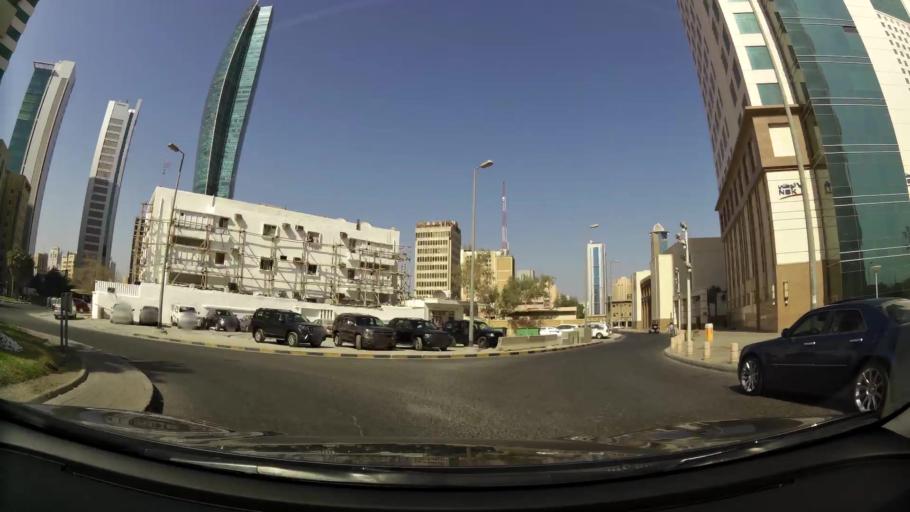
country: KW
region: Al Asimah
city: Kuwait City
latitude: 29.3758
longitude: 47.9904
